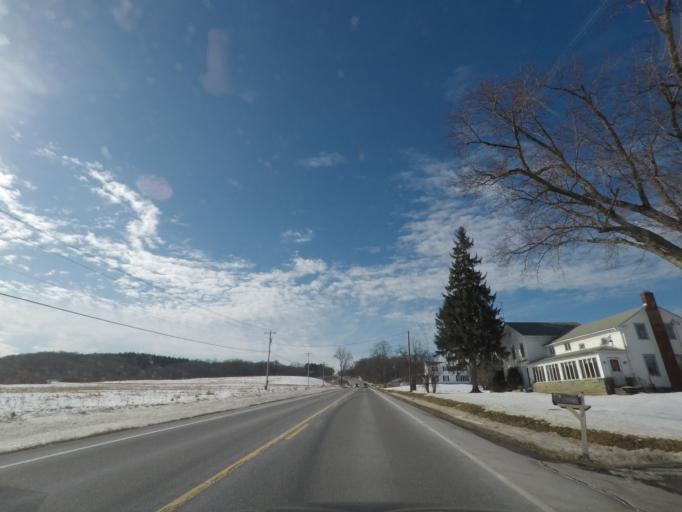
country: US
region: New York
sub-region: Albany County
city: Altamont
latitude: 42.7531
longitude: -74.0582
